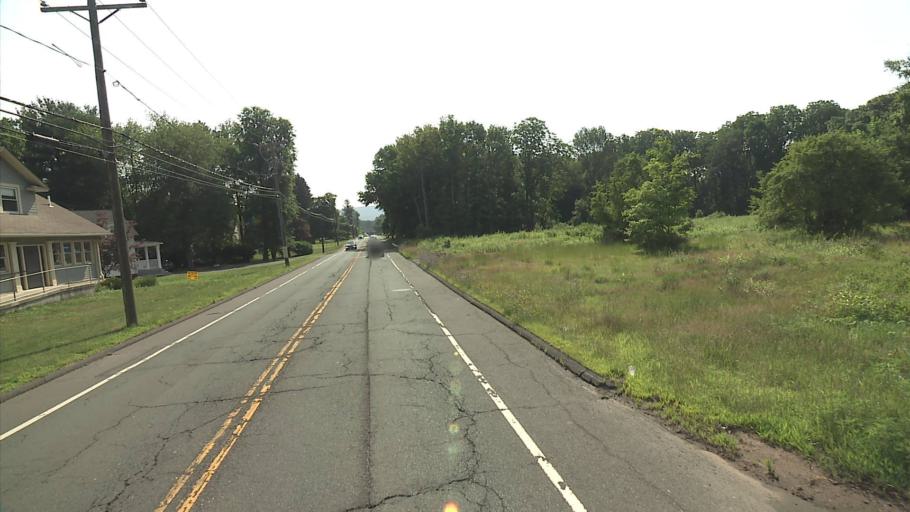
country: US
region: Connecticut
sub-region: New Haven County
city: Cheshire Village
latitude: 41.5645
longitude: -72.8976
